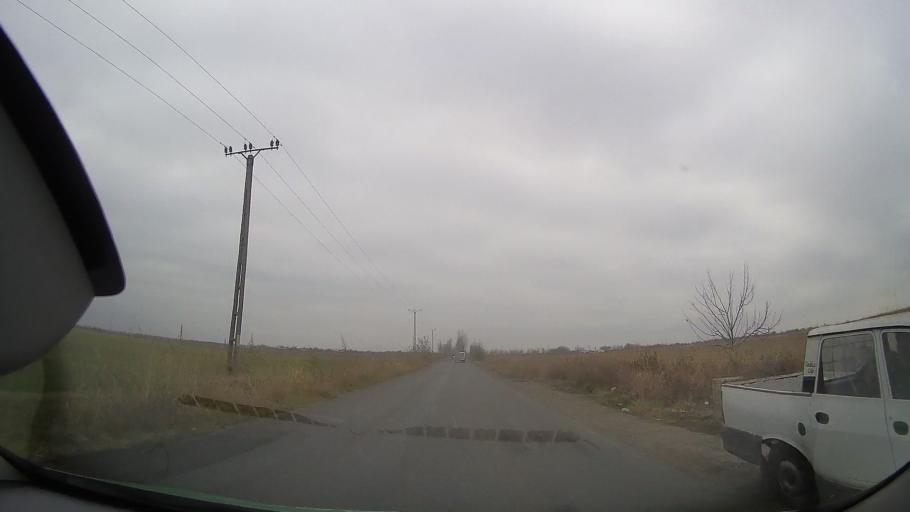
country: RO
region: Buzau
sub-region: Comuna Pogoanele
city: Pogoanele
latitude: 44.9395
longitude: 27.0047
